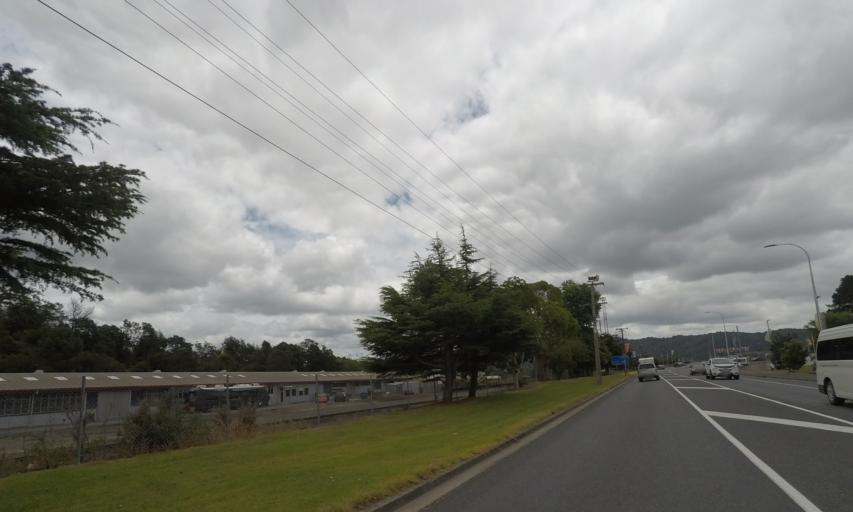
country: NZ
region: Northland
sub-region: Whangarei
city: Whangarei
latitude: -35.7350
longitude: 174.3292
